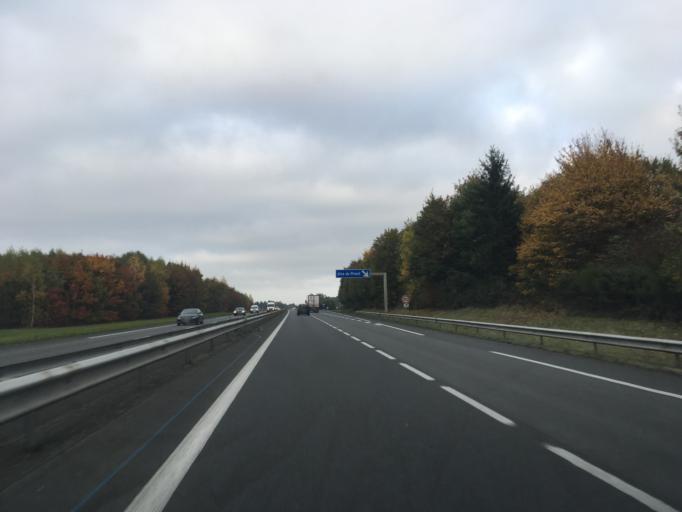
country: FR
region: Pays de la Loire
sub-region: Departement de la Sarthe
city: Noyen-sur-Sarthe
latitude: 47.9092
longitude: -0.0879
